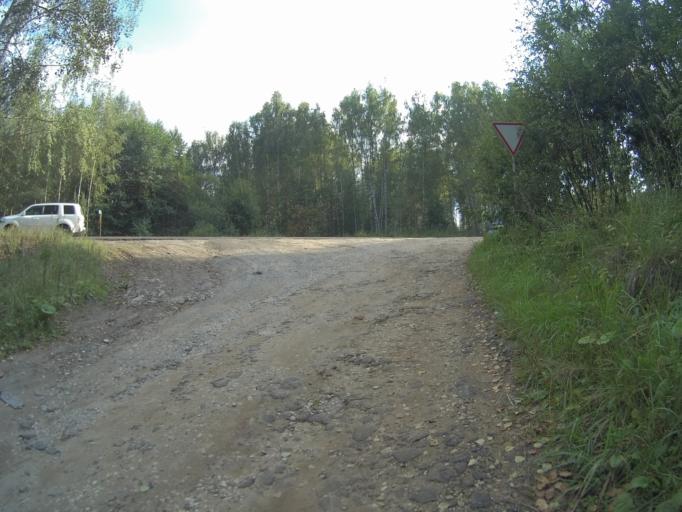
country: RU
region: Vladimir
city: Raduzhnyy
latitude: 56.0017
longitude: 40.2683
